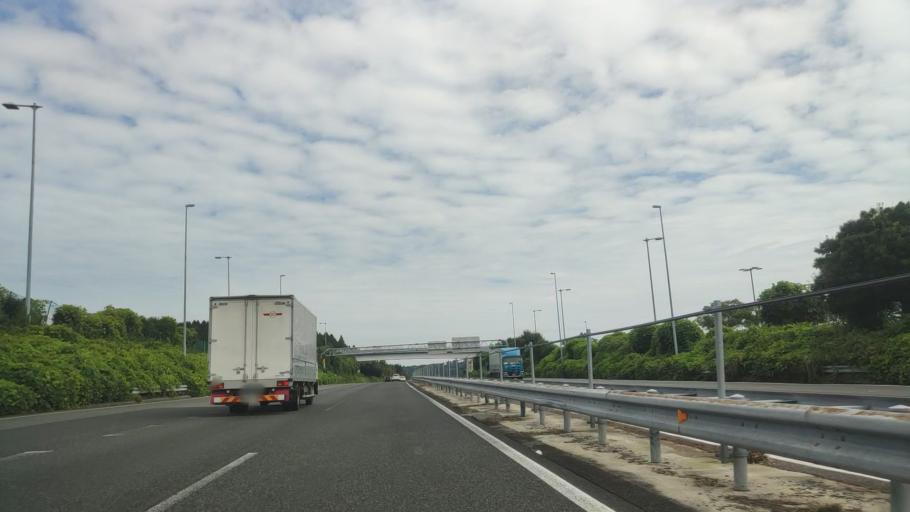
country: JP
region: Mie
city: Kameyama
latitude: 34.8668
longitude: 136.4148
